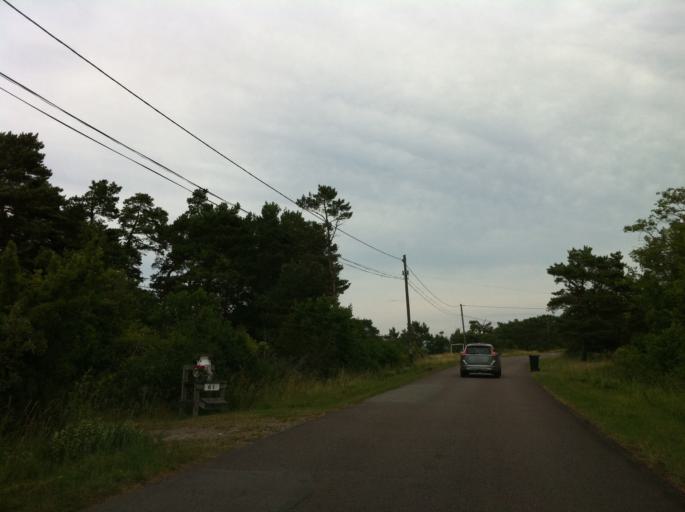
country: SE
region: Kalmar
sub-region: Vasterviks Kommun
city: Vaestervik
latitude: 57.3600
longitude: 17.0666
